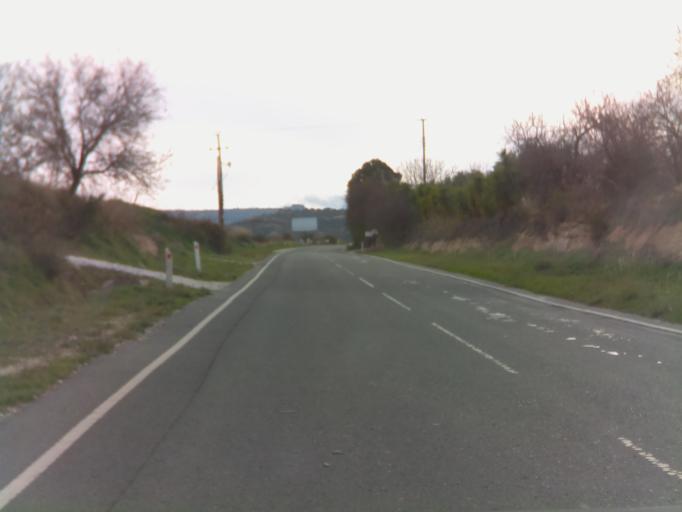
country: CY
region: Pafos
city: Polis
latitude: 35.0219
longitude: 32.4141
